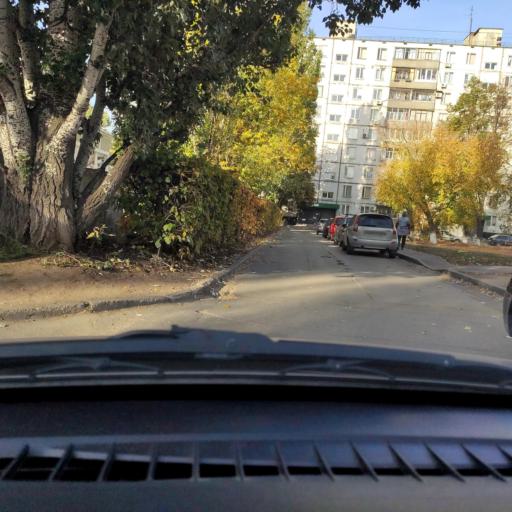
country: RU
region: Samara
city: Tol'yatti
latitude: 53.5113
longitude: 49.2616
